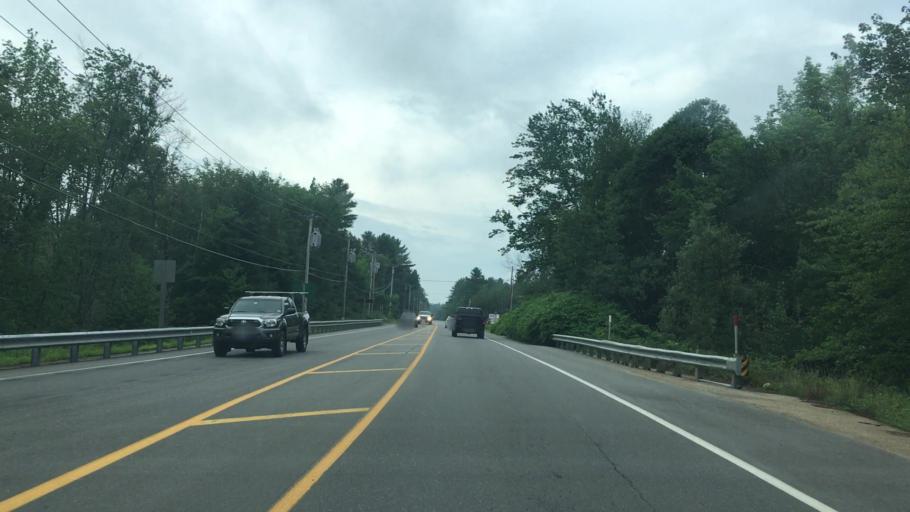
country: US
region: Maine
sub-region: York County
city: Lebanon
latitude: 43.4116
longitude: -70.8691
